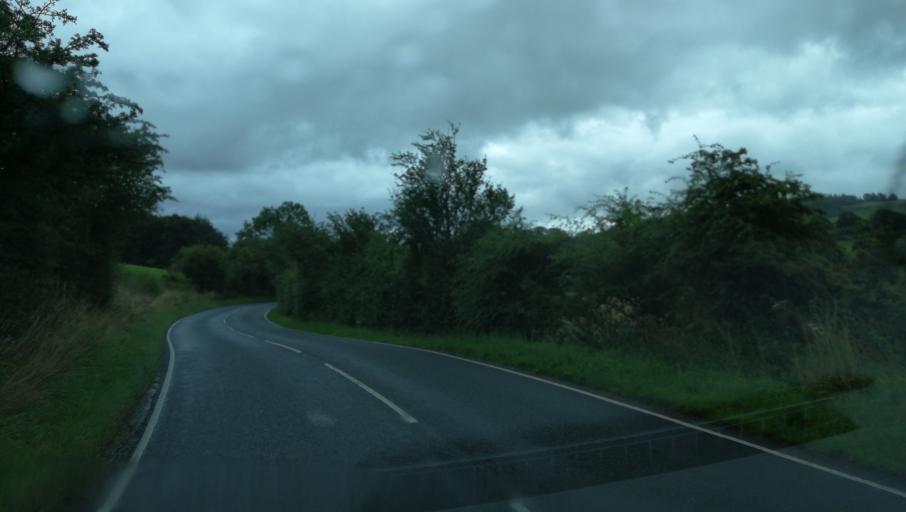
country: GB
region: England
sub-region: Cumbria
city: Penrith
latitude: 54.6234
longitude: -2.8187
